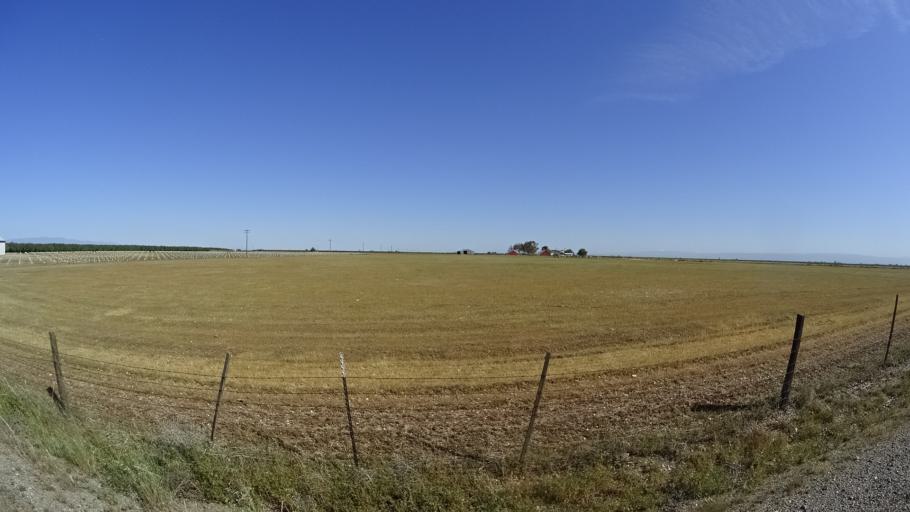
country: US
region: California
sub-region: Glenn County
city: Willows
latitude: 39.6113
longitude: -122.1554
